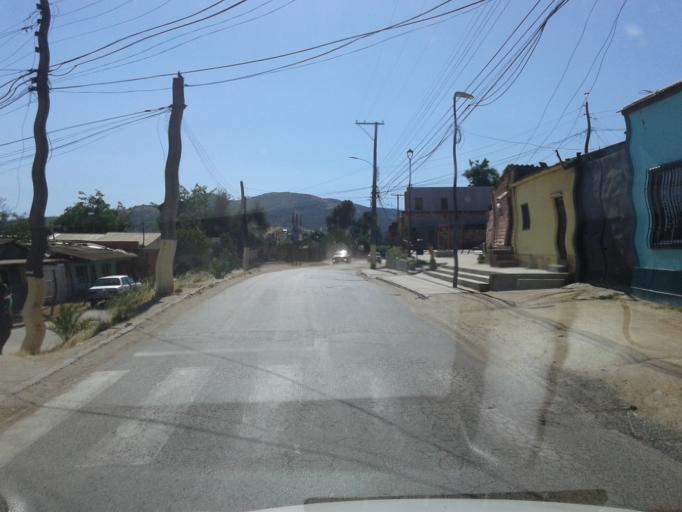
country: CL
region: Valparaiso
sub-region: Provincia de Quillota
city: Quillota
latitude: -32.8759
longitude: -71.2542
